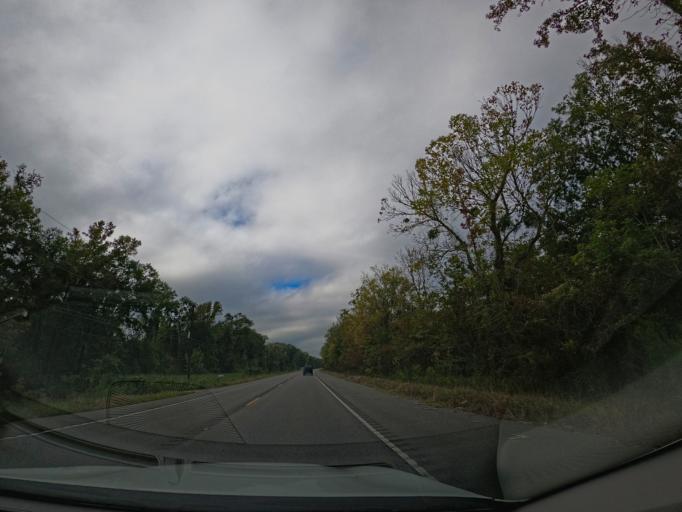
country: US
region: Louisiana
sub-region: Saint Mary Parish
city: Amelia
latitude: 29.6787
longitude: -91.0092
